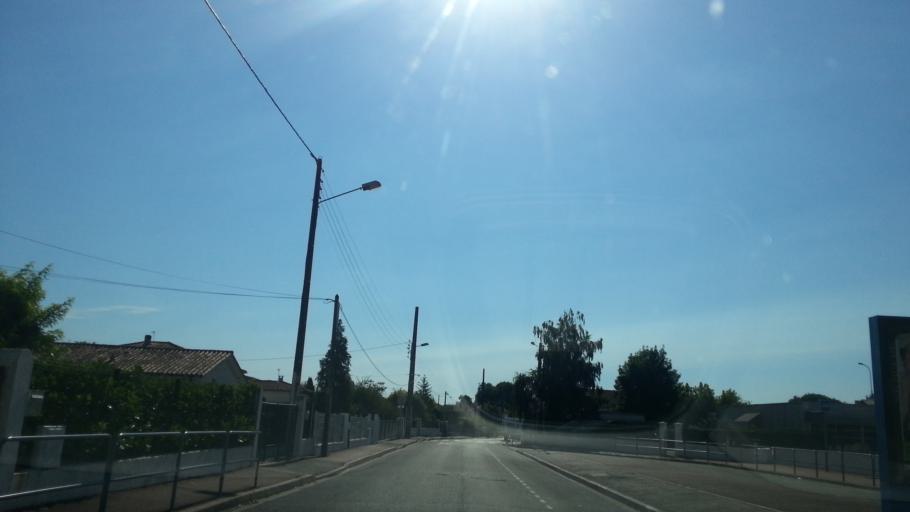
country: FR
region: Aquitaine
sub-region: Departement de la Gironde
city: Villenave-d'Ornon
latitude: 44.7670
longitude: -0.5687
